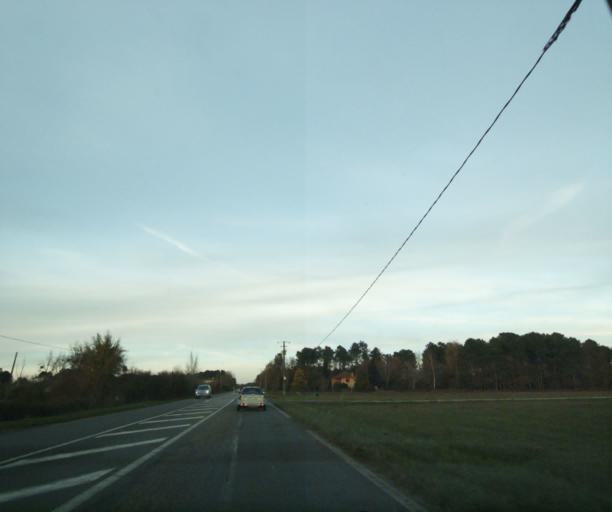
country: FR
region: Aquitaine
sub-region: Departement de la Gironde
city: Bazas
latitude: 44.4591
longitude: -0.2319
